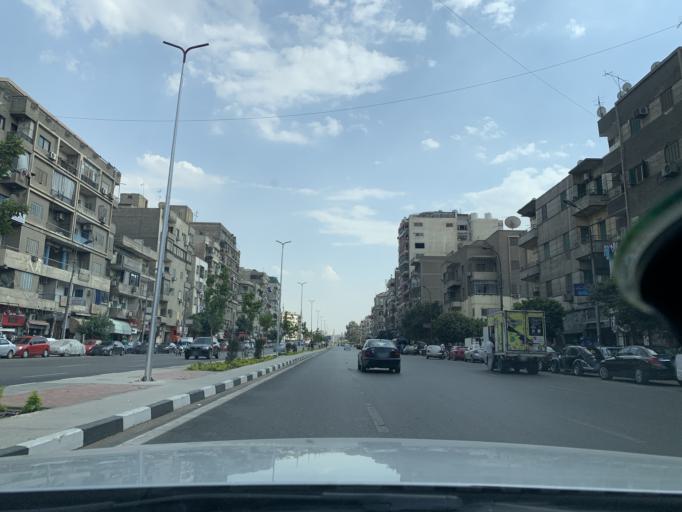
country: EG
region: Muhafazat al Qahirah
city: Cairo
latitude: 30.1037
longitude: 31.3435
